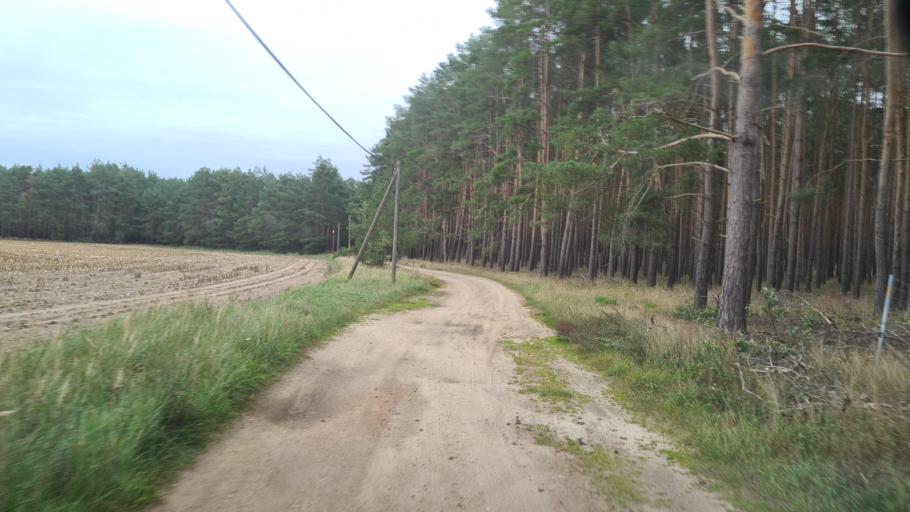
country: DE
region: Brandenburg
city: Golssen
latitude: 51.9519
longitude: 13.5720
